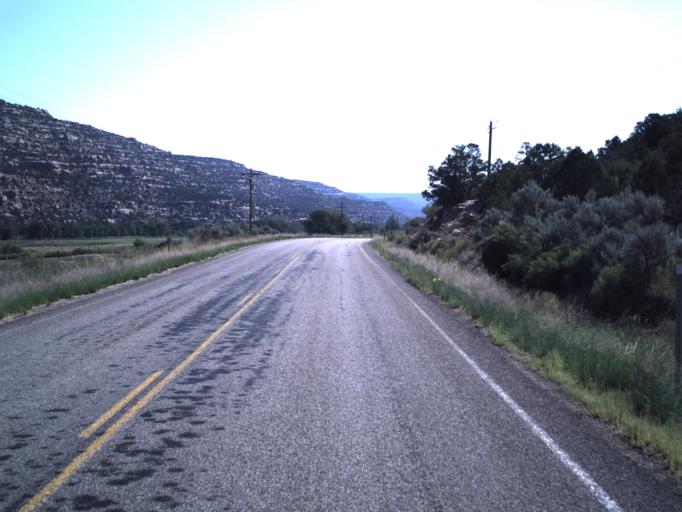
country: US
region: Utah
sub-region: Duchesne County
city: Duchesne
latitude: 40.2960
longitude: -110.5904
